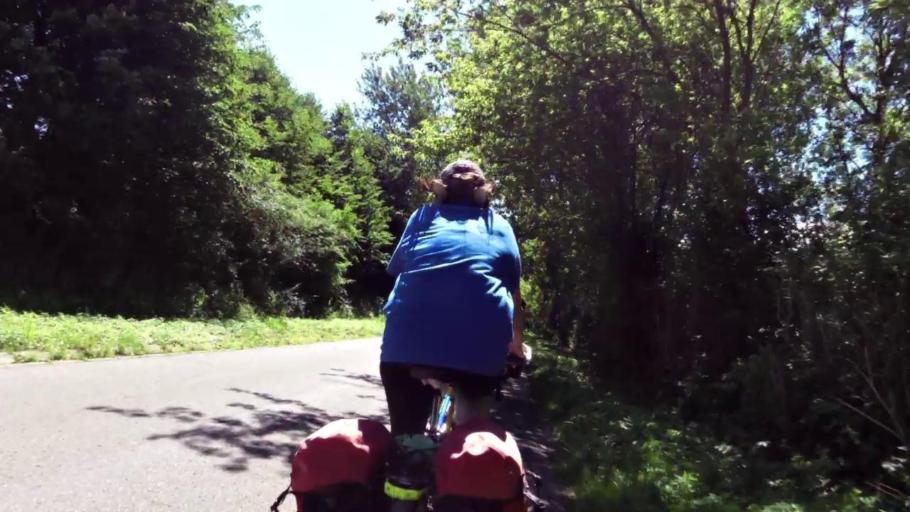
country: PL
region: West Pomeranian Voivodeship
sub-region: Koszalin
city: Koszalin
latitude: 54.2859
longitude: 16.2094
